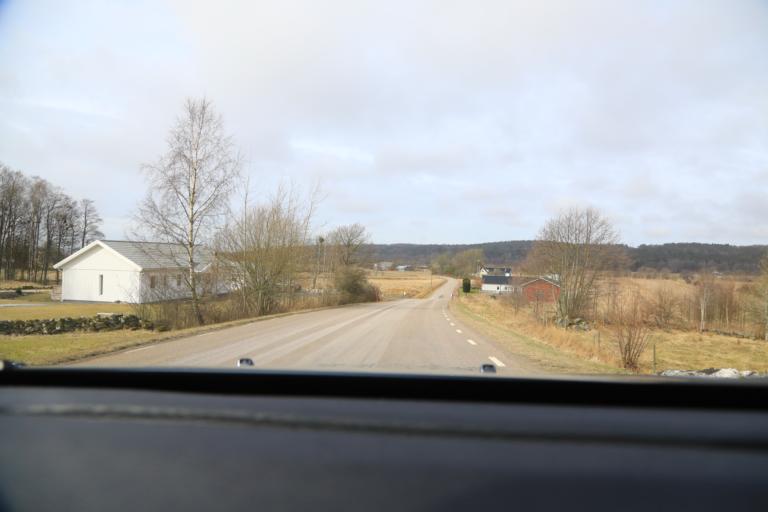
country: SE
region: Halland
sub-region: Varbergs Kommun
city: Veddige
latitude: 57.2261
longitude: 12.2481
